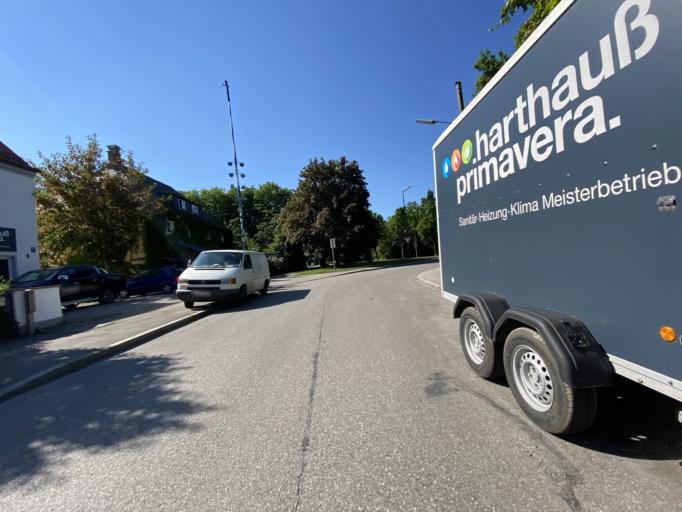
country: DE
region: Bavaria
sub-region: Upper Bavaria
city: Pasing
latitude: 48.1366
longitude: 11.4626
